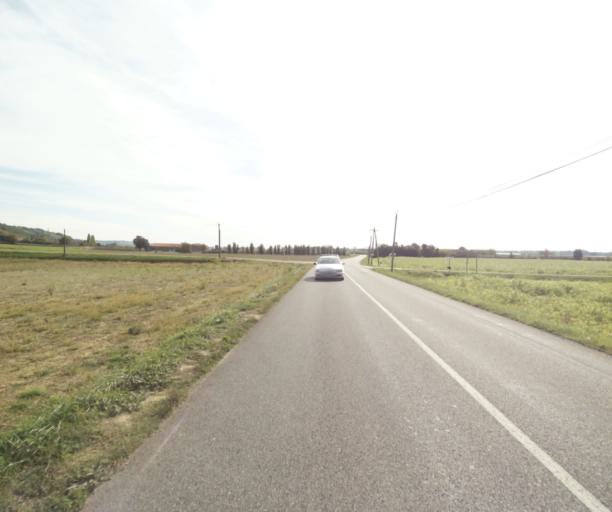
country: FR
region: Midi-Pyrenees
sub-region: Departement du Tarn-et-Garonne
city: Corbarieu
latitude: 43.9380
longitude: 1.3750
